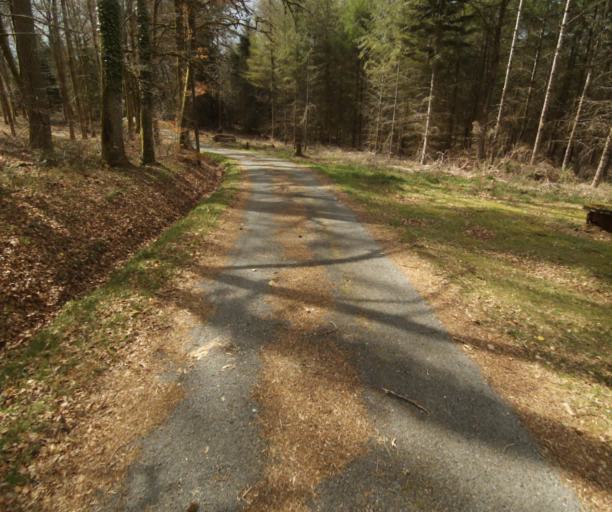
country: FR
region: Limousin
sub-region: Departement de la Correze
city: Correze
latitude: 45.2686
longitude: 1.9774
